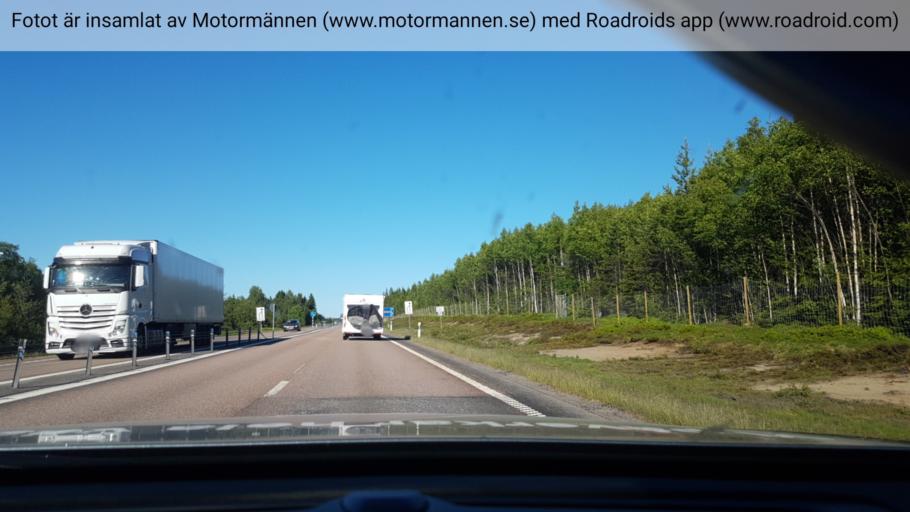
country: SE
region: Vaesternorrland
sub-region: Haernoesands Kommun
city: Haernoesand
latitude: 62.6078
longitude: 17.8274
